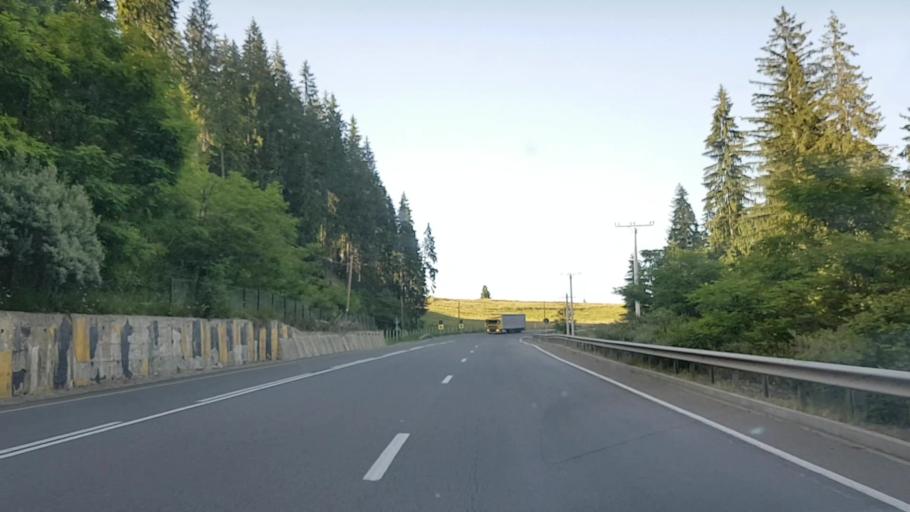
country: RO
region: Bistrita-Nasaud
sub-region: Comuna Lunca Ilvei
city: Lunca Ilvei
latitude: 47.2286
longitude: 24.9765
